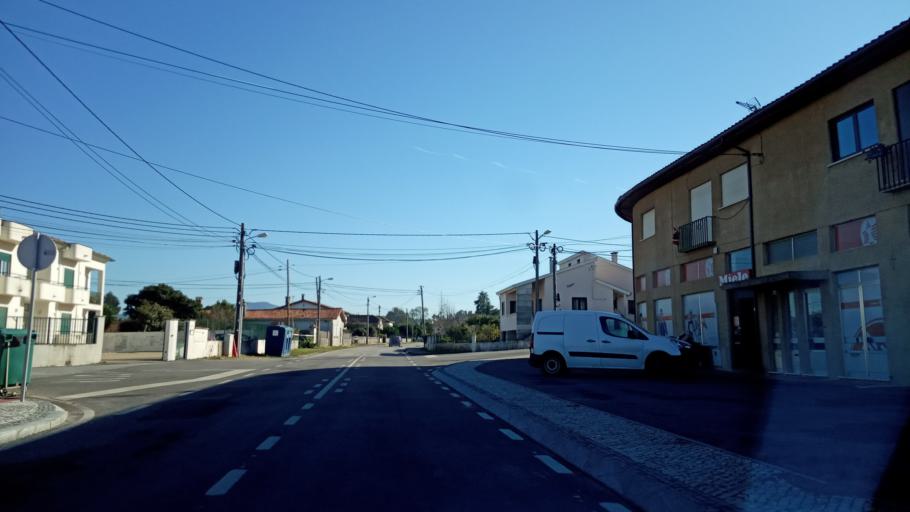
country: PT
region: Aveiro
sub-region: Anadia
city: Anadia
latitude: 40.4309
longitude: -8.4299
